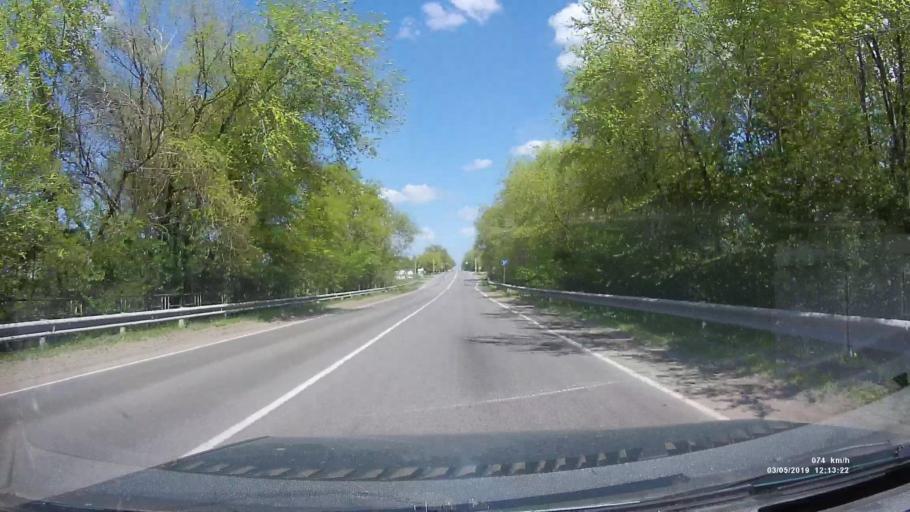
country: RU
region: Rostov
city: Melikhovskaya
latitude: 47.3319
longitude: 40.5544
